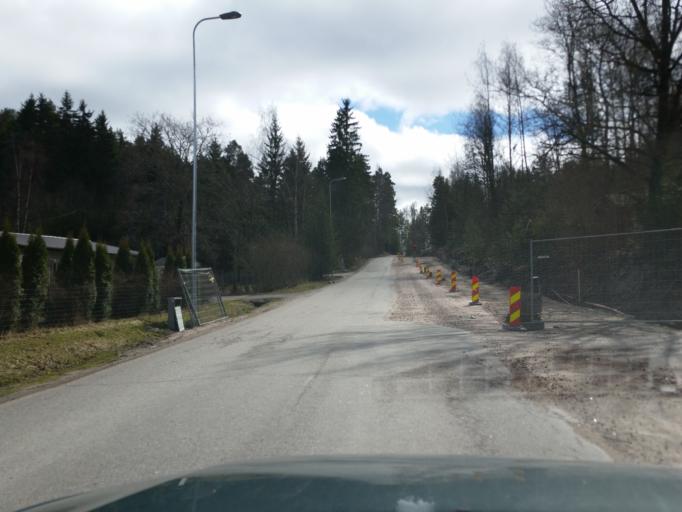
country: FI
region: Uusimaa
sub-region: Helsinki
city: Vihti
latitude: 60.4091
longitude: 24.3305
